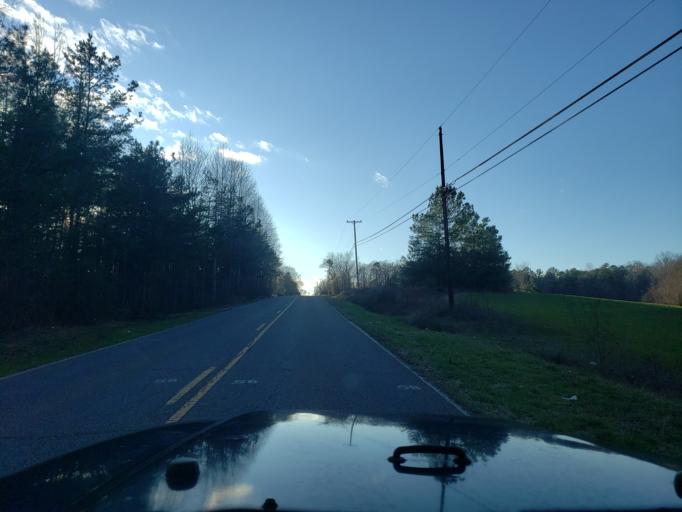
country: US
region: North Carolina
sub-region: Cleveland County
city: Shelby
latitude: 35.4152
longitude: -81.5790
